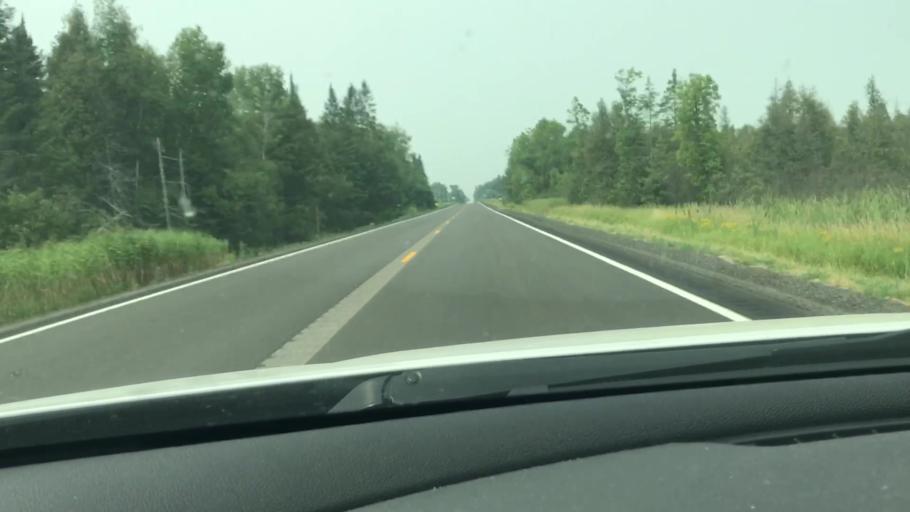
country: US
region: Minnesota
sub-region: Itasca County
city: Cohasset
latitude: 47.3530
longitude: -93.8443
